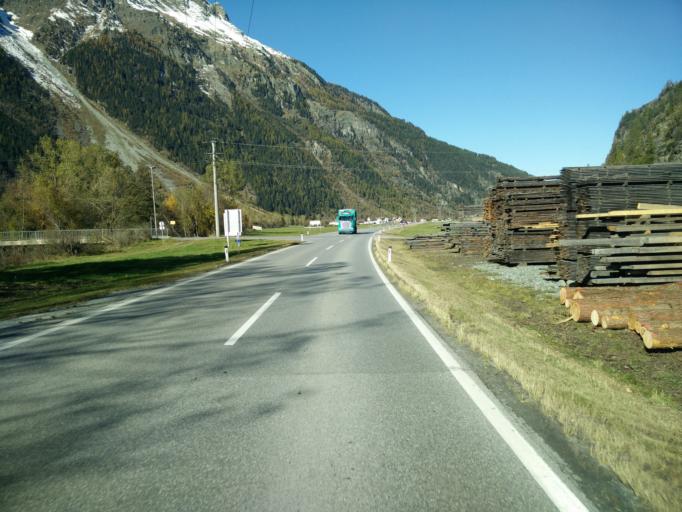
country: AT
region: Tyrol
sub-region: Politischer Bezirk Imst
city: Soelden
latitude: 47.0451
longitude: 10.9705
